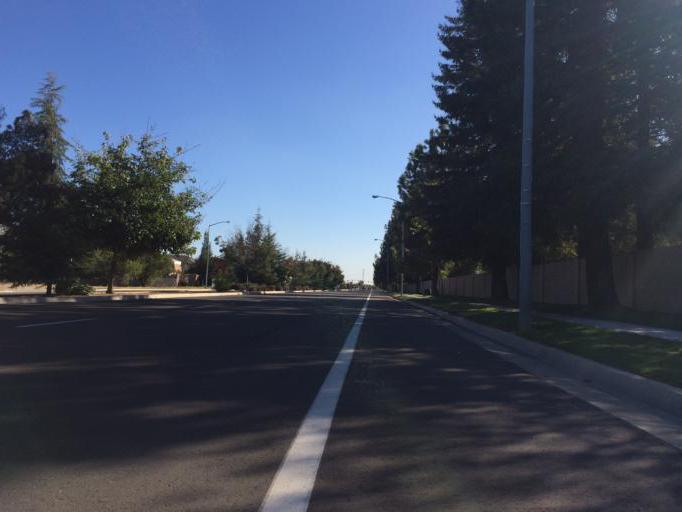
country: US
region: California
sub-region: Fresno County
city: Clovis
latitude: 36.8348
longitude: -119.6641
